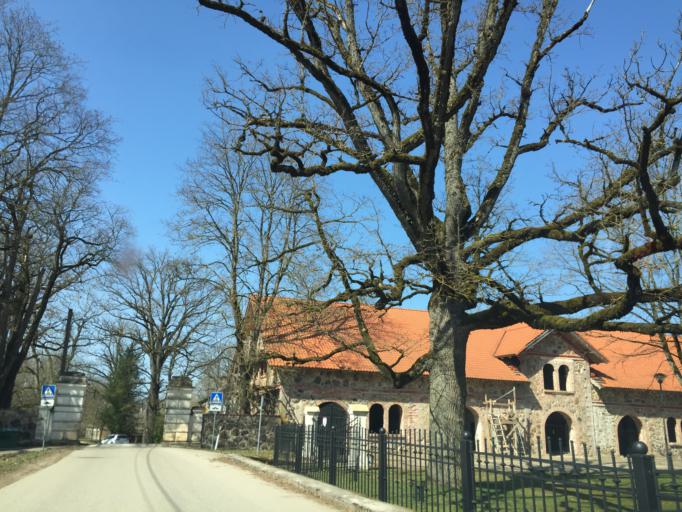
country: LV
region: Malpils
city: Malpils
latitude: 57.0058
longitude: 24.9484
